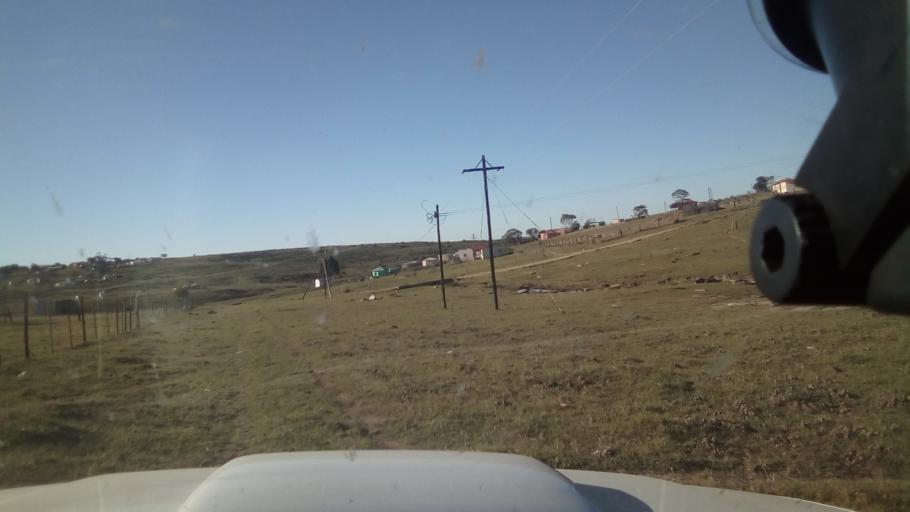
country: ZA
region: Eastern Cape
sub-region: Buffalo City Metropolitan Municipality
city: Bhisho
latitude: -32.9485
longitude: 27.2891
